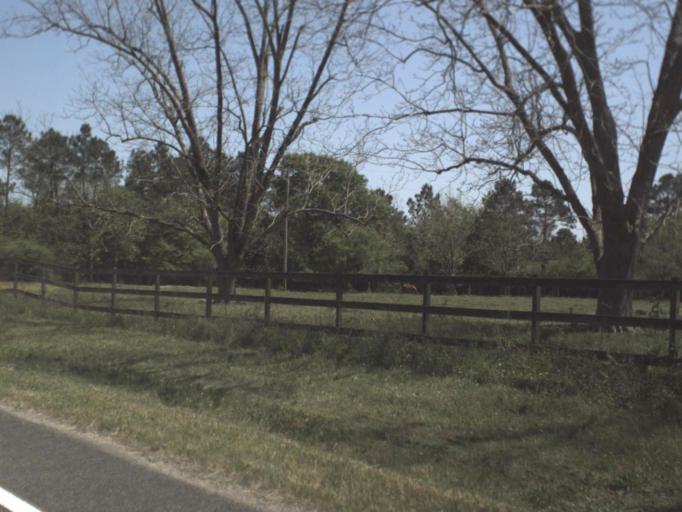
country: US
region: Alabama
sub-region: Escambia County
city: East Brewton
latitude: 30.8997
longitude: -87.0235
